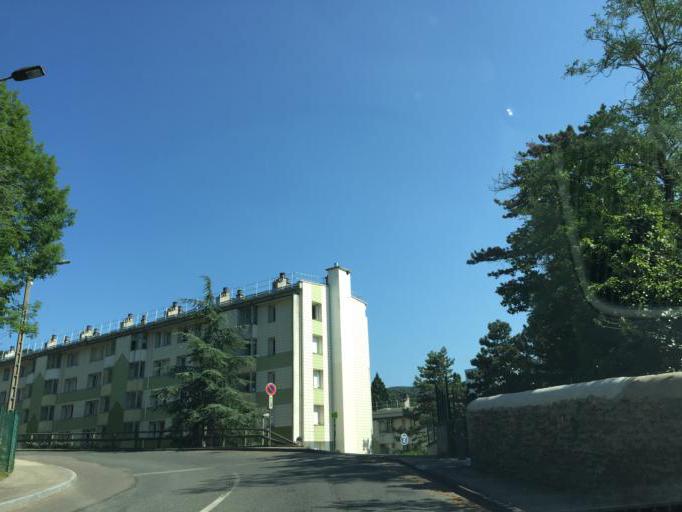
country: FR
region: Rhone-Alpes
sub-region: Departement de la Loire
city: Saint-Etienne
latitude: 45.4173
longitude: 4.4068
